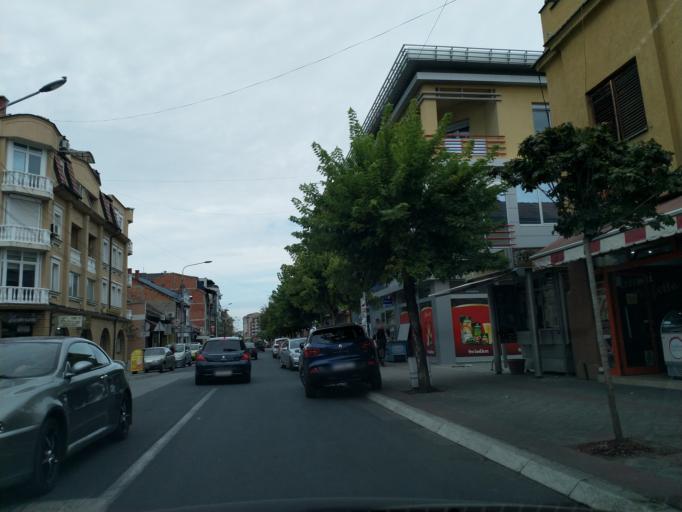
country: RS
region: Central Serbia
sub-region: Pomoravski Okrug
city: Jagodina
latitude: 43.9762
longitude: 21.2633
